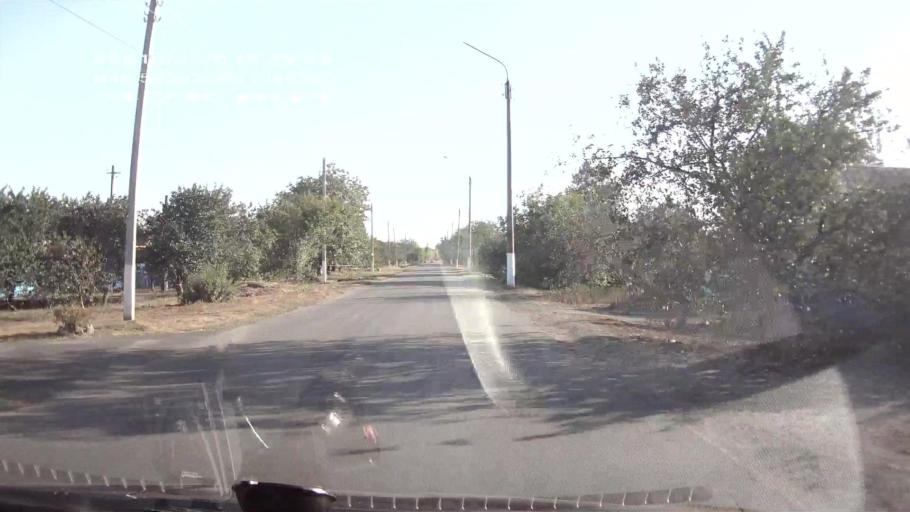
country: RU
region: Rostov
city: Gigant
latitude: 46.5228
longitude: 41.1907
